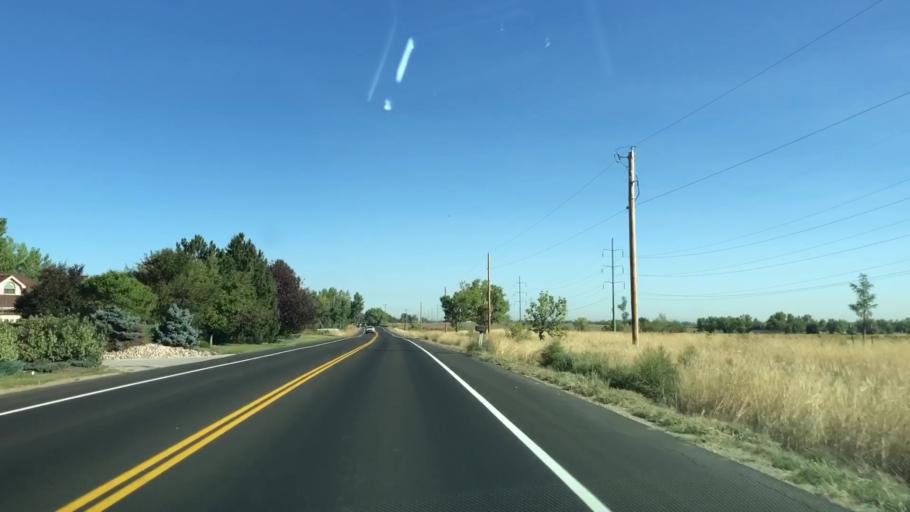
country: US
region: Colorado
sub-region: Larimer County
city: Loveland
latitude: 40.4352
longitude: -105.0454
